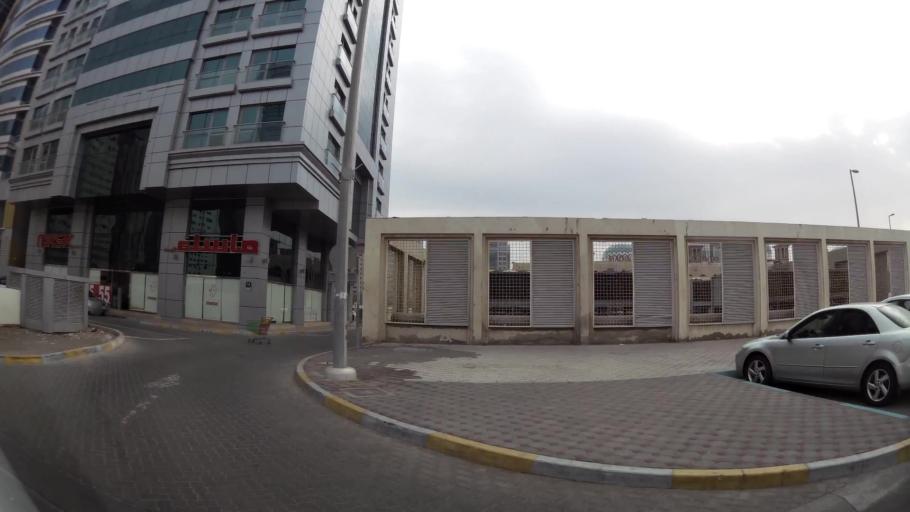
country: AE
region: Abu Dhabi
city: Abu Dhabi
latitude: 24.4837
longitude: 54.3639
